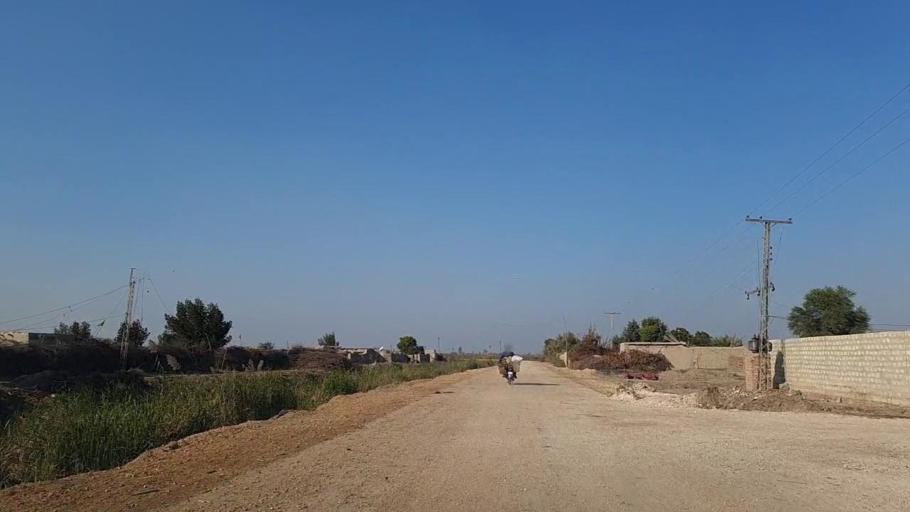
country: PK
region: Sindh
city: Bandhi
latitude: 26.6053
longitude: 68.3132
